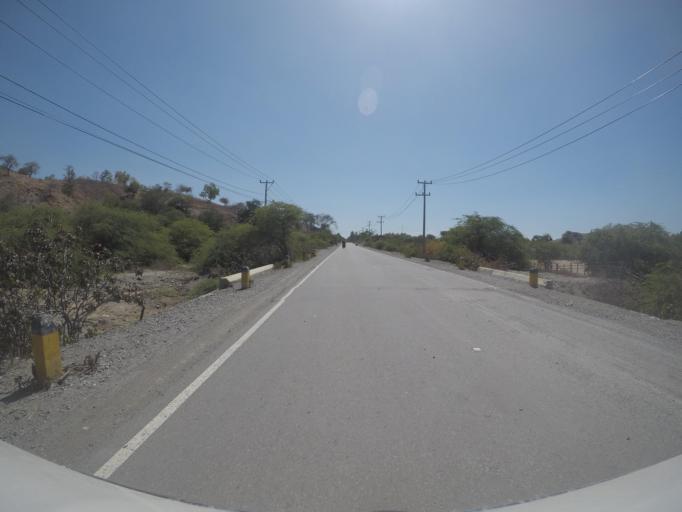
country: TL
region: Liquica
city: Liquica
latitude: -8.5669
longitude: 125.4272
